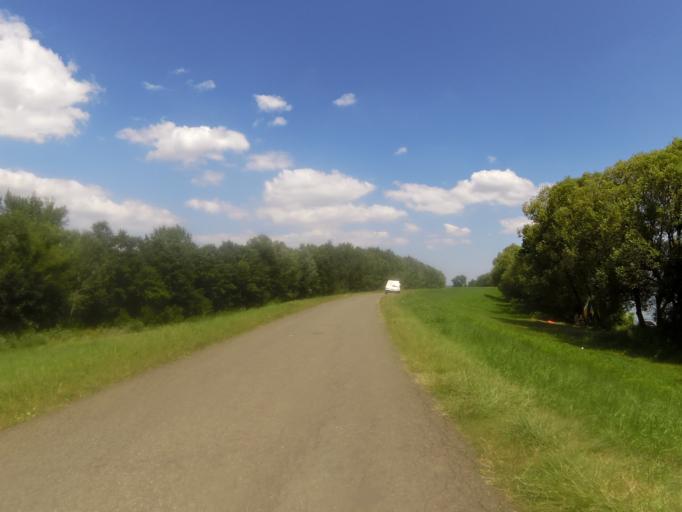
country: HU
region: Heves
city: Tiszanana
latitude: 47.5600
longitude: 20.6085
